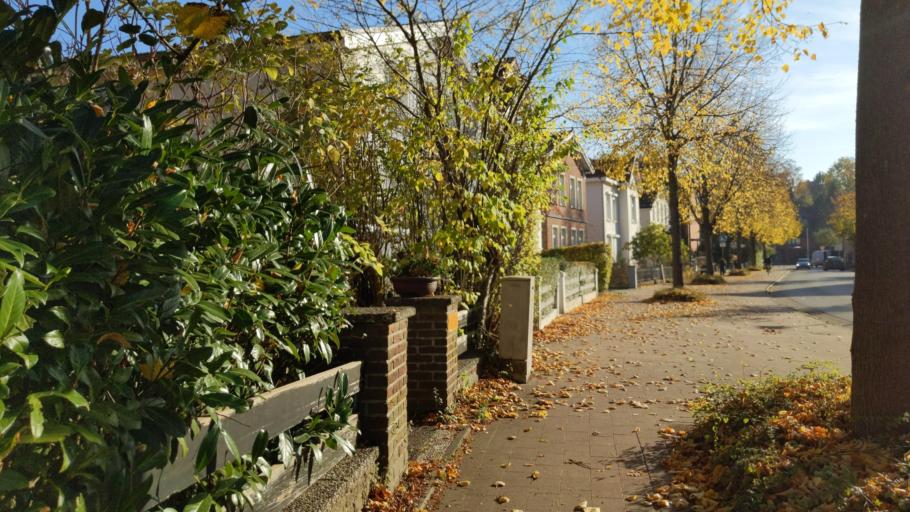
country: DE
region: Schleswig-Holstein
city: Eutin
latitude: 54.1433
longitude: 10.6122
